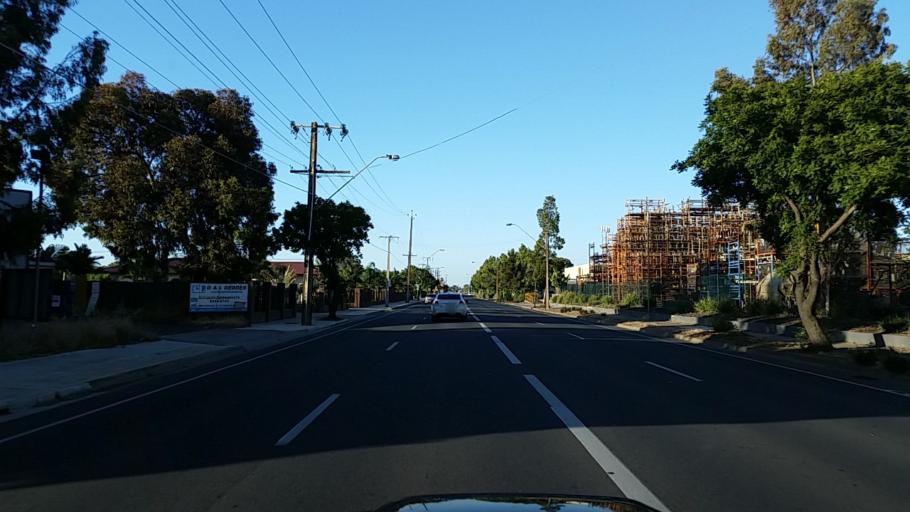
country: AU
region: South Australia
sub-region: Charles Sturt
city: Albert Park
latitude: -34.8733
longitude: 138.5284
